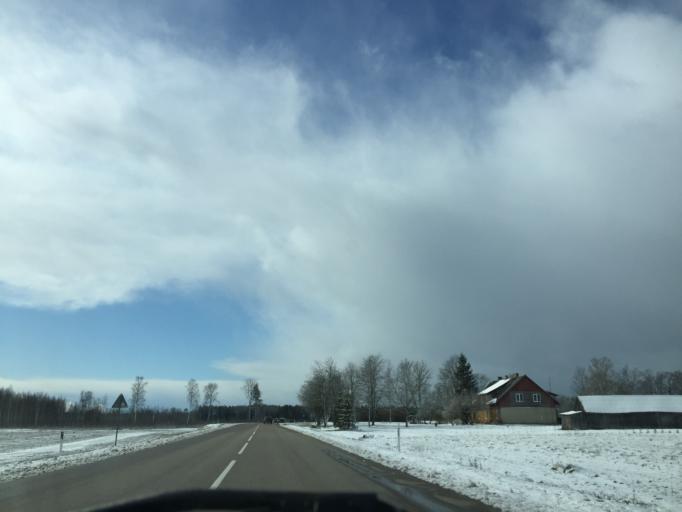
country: LV
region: Talsu Rajons
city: Stende
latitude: 57.2112
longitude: 22.4746
